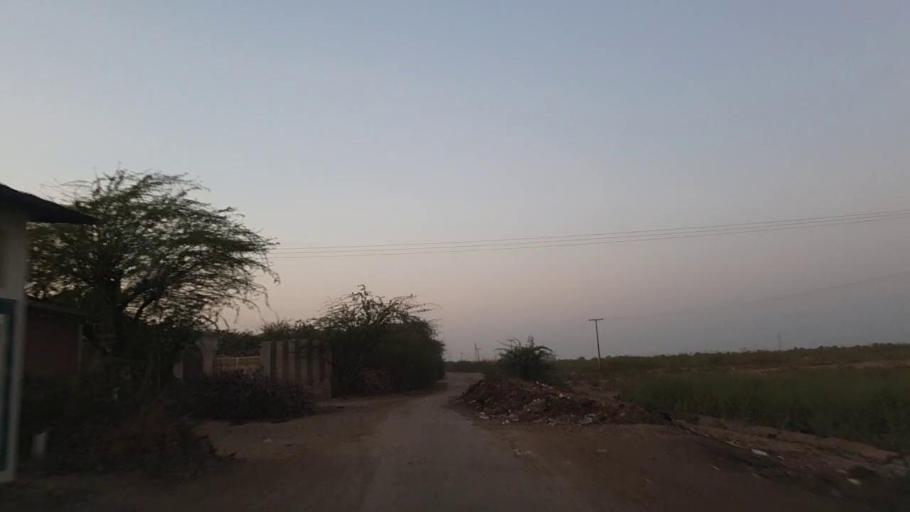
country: PK
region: Sindh
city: Naukot
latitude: 24.8882
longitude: 69.3852
